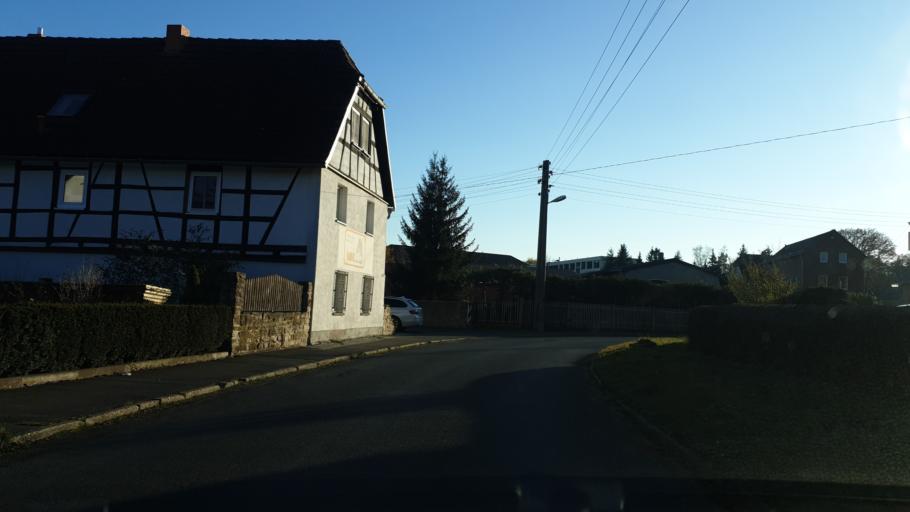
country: DE
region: Thuringia
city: Hartmannsdorf
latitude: 50.9746
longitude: 11.9753
